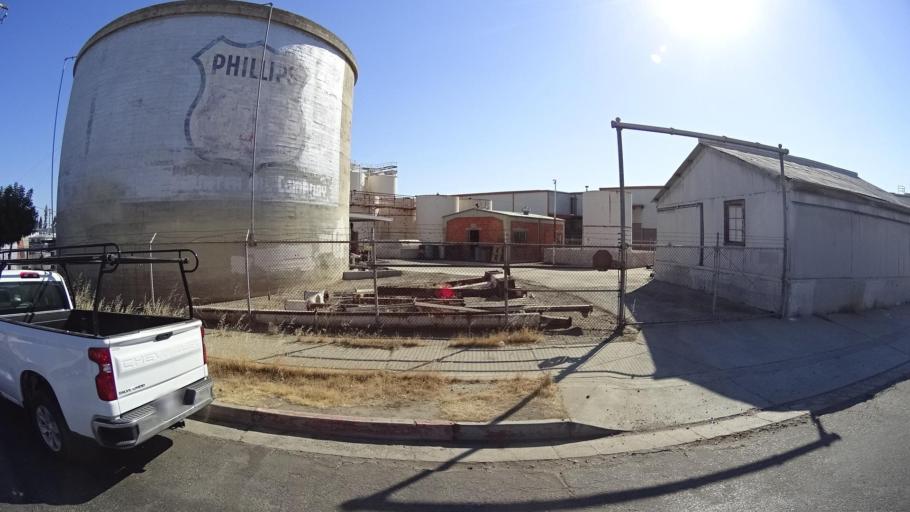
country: US
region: California
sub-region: Fresno County
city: Fresno
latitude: 36.7291
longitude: -119.7775
